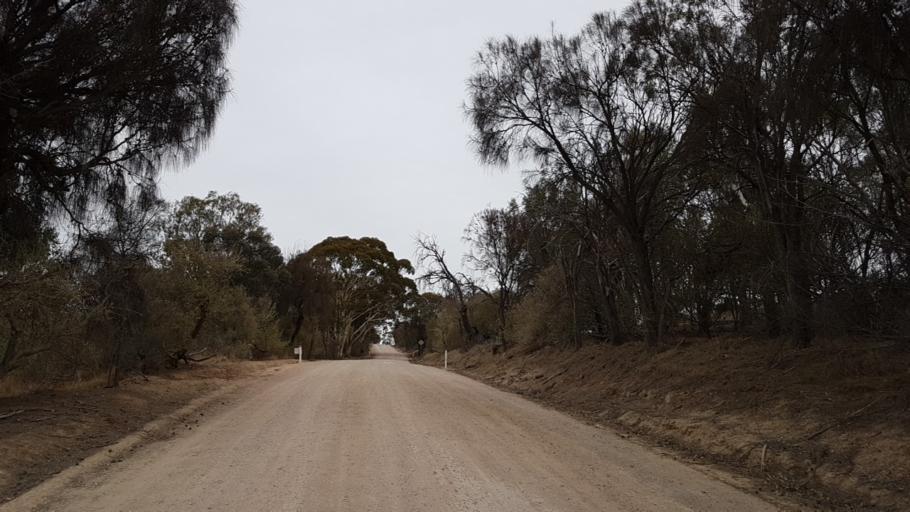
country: AU
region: South Australia
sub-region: Mount Barker
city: Nairne
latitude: -34.9991
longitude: 139.0071
